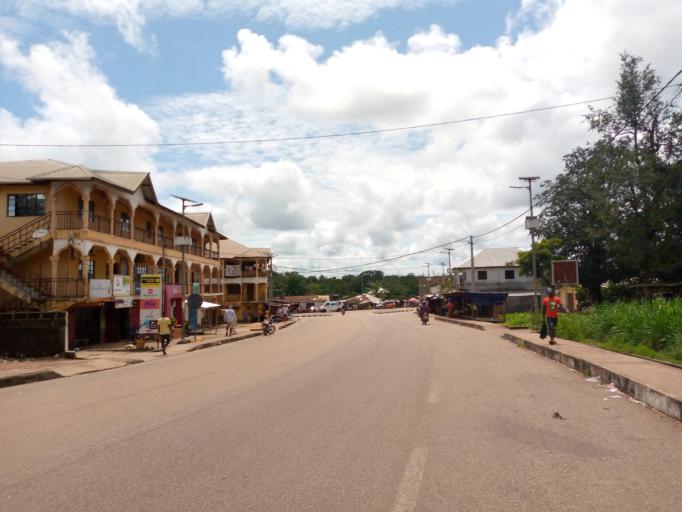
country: SL
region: Northern Province
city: Magburaka
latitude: 8.7209
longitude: -11.9359
